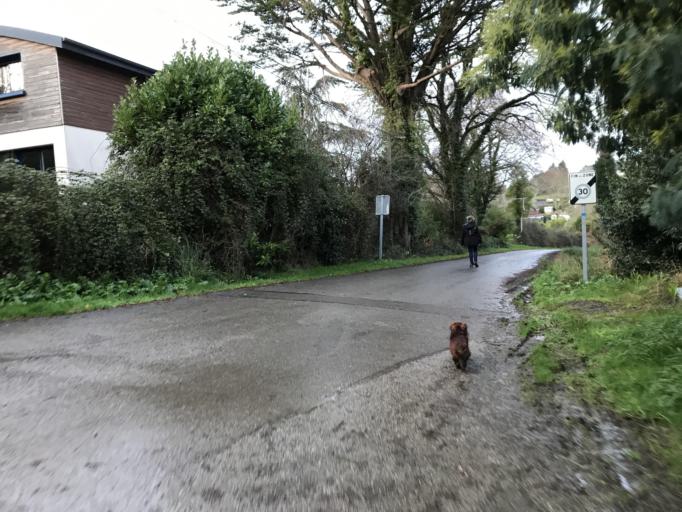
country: FR
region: Brittany
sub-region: Departement du Finistere
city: Logonna-Daoulas
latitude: 48.3167
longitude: -4.3162
